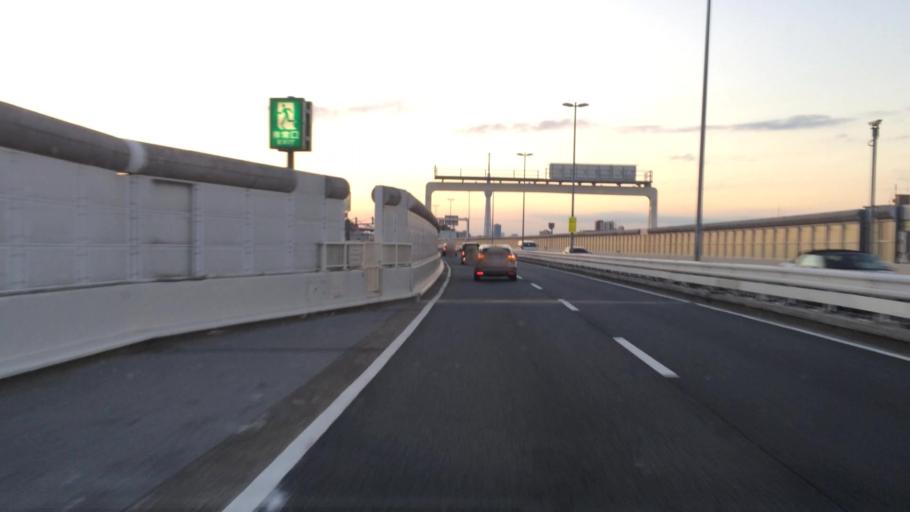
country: JP
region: Tokyo
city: Urayasu
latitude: 35.6987
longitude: 139.8725
